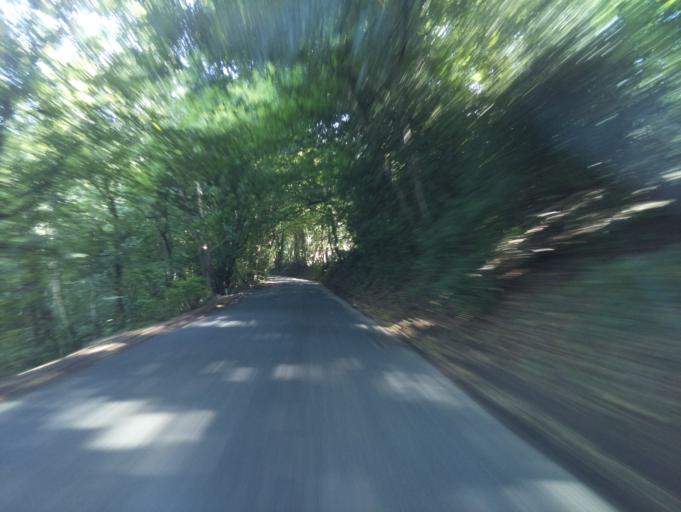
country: GB
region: England
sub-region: Gloucestershire
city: Dursley
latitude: 51.6746
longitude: -2.2953
